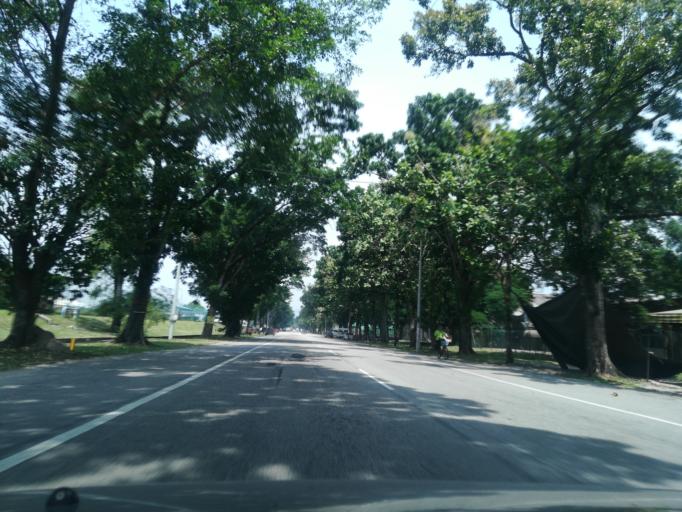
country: MY
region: Kedah
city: Kulim
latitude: 5.4091
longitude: 100.5589
